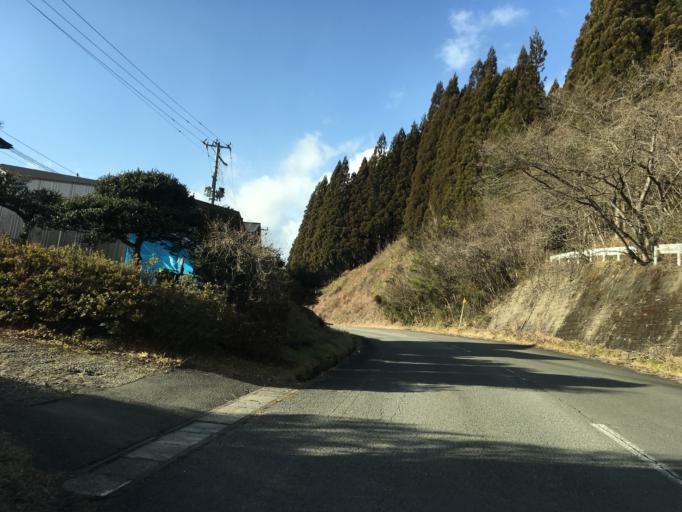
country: JP
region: Miyagi
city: Furukawa
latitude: 38.7997
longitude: 140.8367
